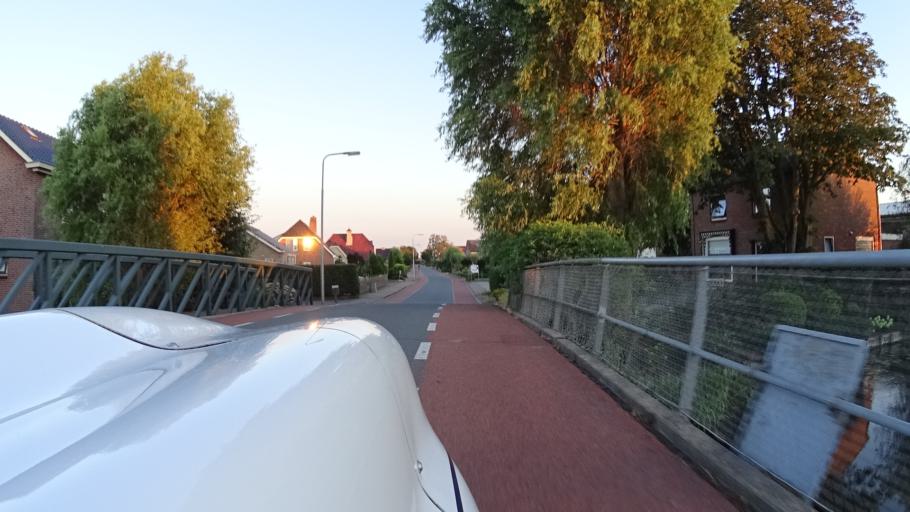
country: NL
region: South Holland
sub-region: Gemeente Kaag en Braassem
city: Oude Wetering
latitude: 52.1872
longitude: 4.6128
